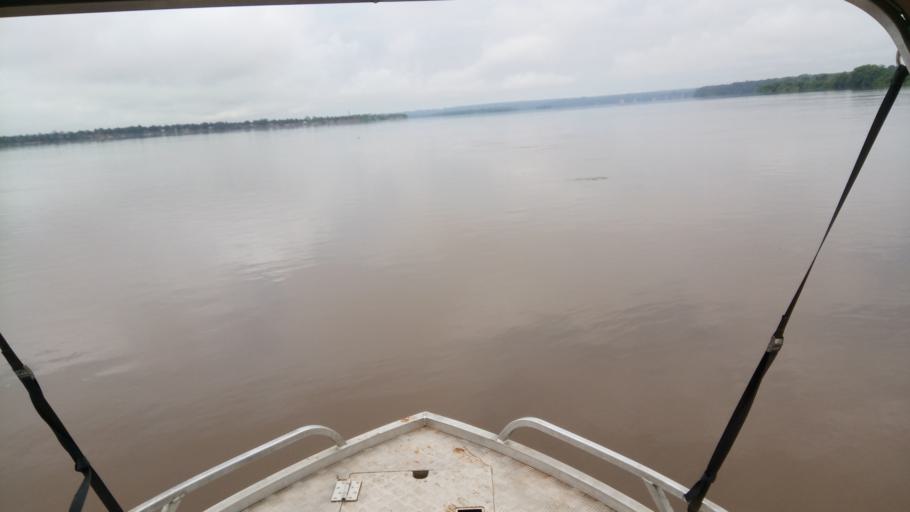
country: CD
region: Eastern Province
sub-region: Sous-Region de la Tshopo
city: Yangambi
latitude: 0.6953
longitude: 24.5827
